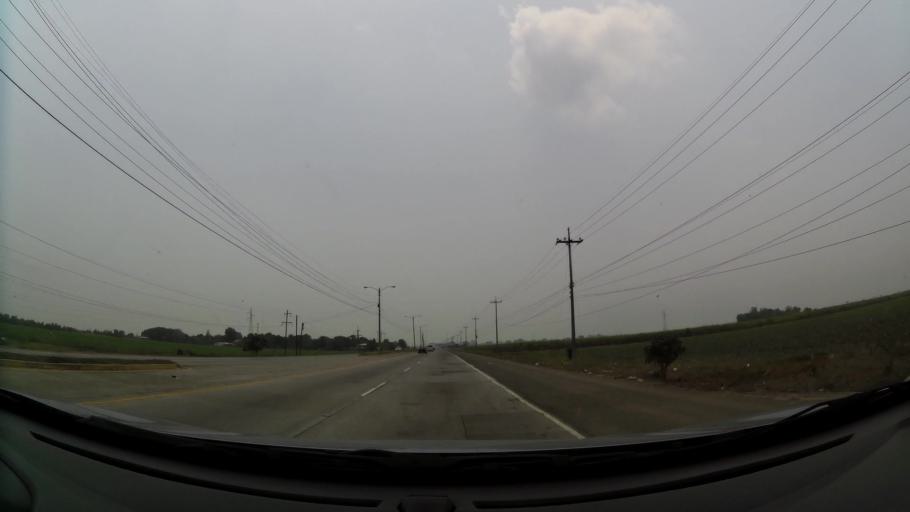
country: HN
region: Cortes
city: La Lima
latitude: 15.4117
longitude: -87.8673
